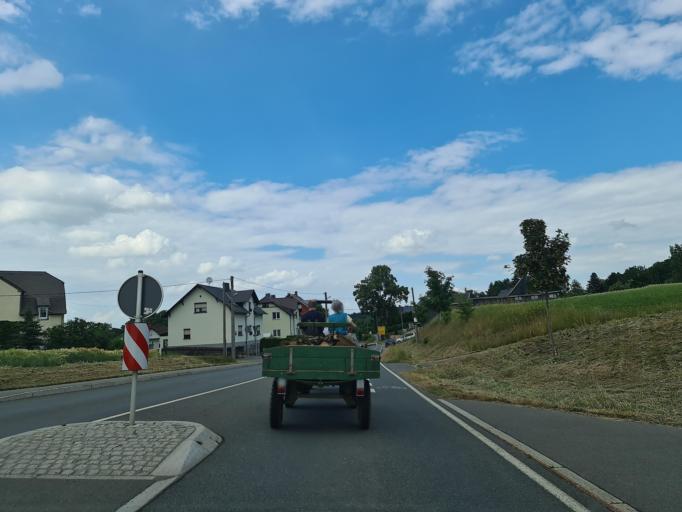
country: DE
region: Saxony
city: Pohl
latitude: 50.5272
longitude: 12.1770
